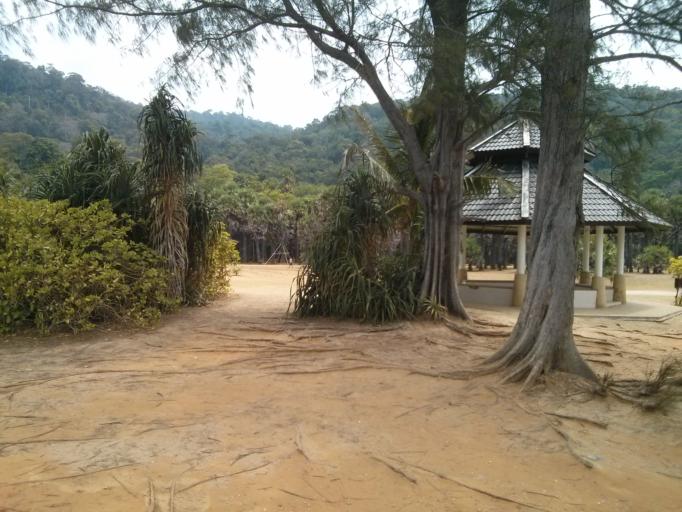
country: TH
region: Krabi
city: Ko Lanta
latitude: 7.4692
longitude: 99.0983
